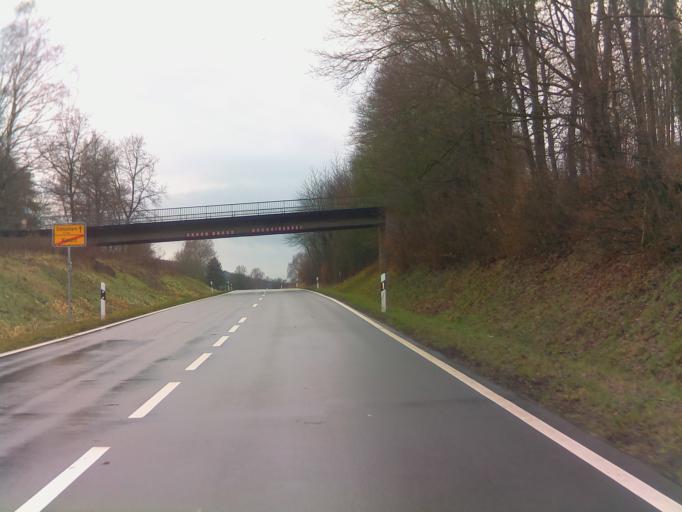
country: DE
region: Hesse
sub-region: Regierungsbezirk Kassel
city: Flieden
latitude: 50.4006
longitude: 9.5451
